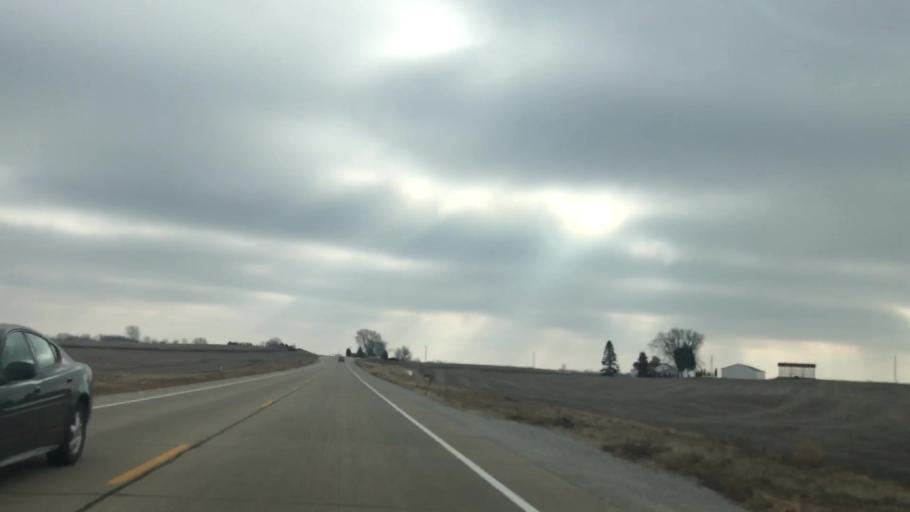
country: US
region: Wisconsin
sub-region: Dodge County
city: Beaver Dam
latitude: 43.4804
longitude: -88.7838
